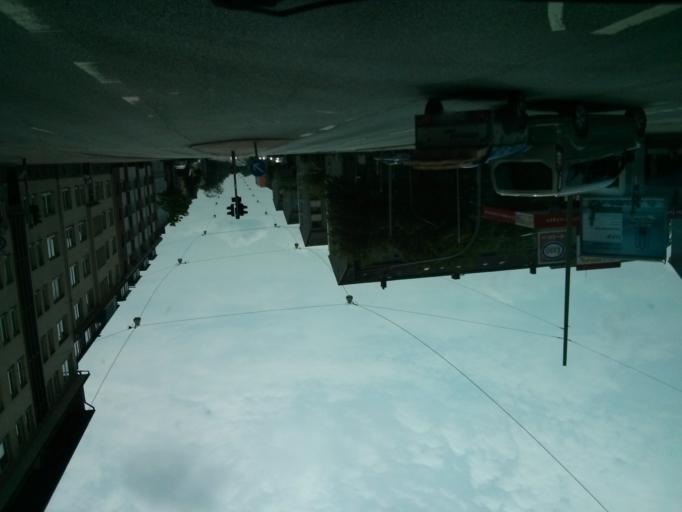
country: DE
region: Bremen
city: Bremerhaven
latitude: 53.5295
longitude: 8.5896
